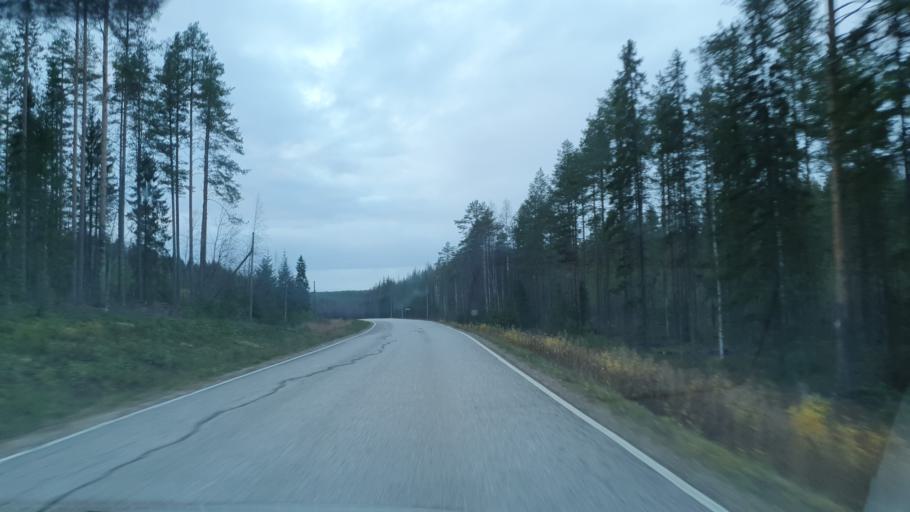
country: FI
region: Kainuu
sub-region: Kajaani
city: Ristijaervi
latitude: 64.4253
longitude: 28.3954
